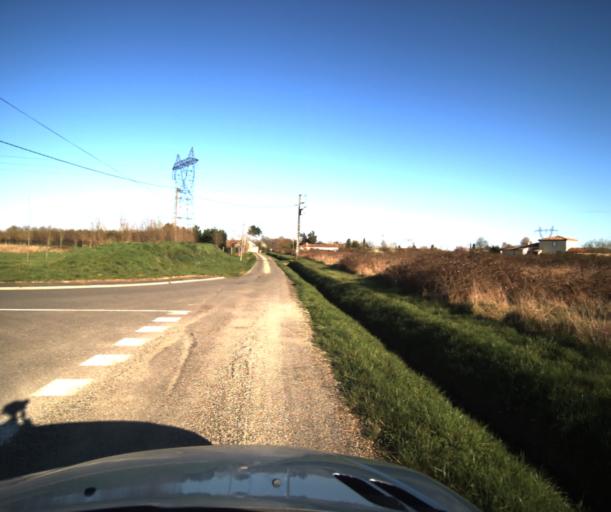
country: FR
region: Midi-Pyrenees
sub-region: Departement du Tarn-et-Garonne
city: Bressols
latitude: 43.9716
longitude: 1.3181
